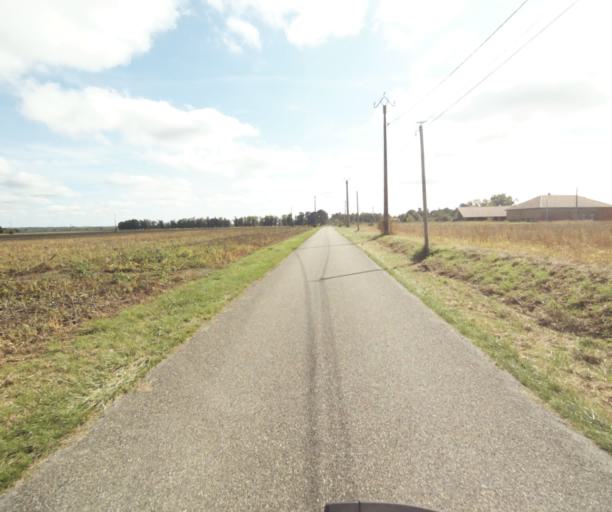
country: FR
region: Midi-Pyrenees
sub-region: Departement du Tarn-et-Garonne
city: Finhan
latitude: 43.9324
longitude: 1.2154
